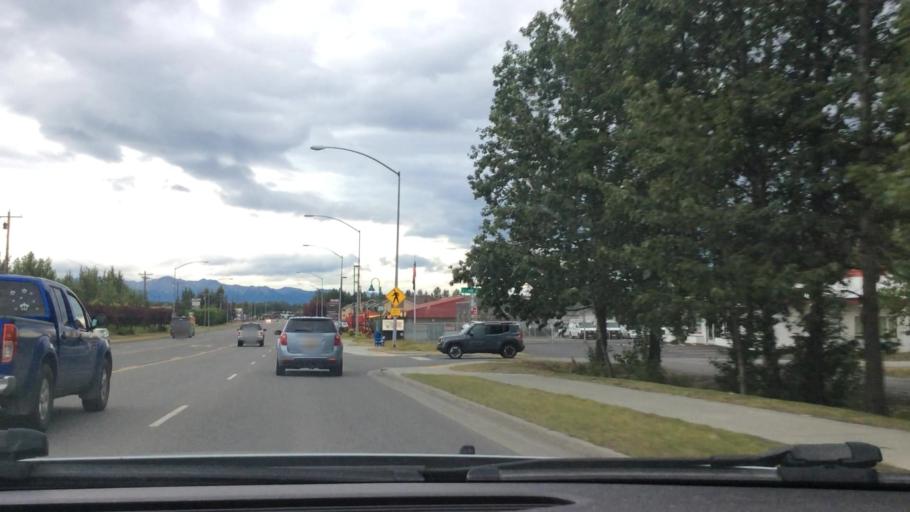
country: US
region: Alaska
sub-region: Anchorage Municipality
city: Anchorage
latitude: 61.1722
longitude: -149.8383
